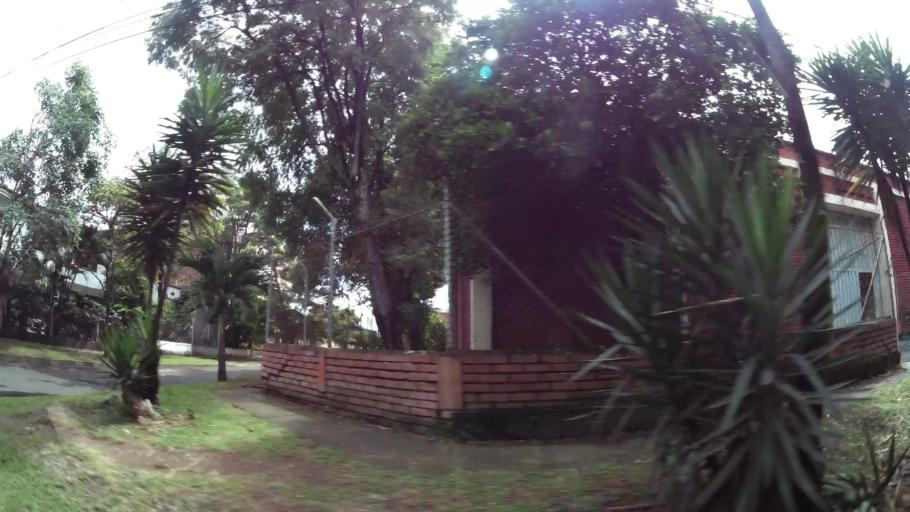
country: CO
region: Valle del Cauca
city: Cali
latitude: 3.3933
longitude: -76.5477
